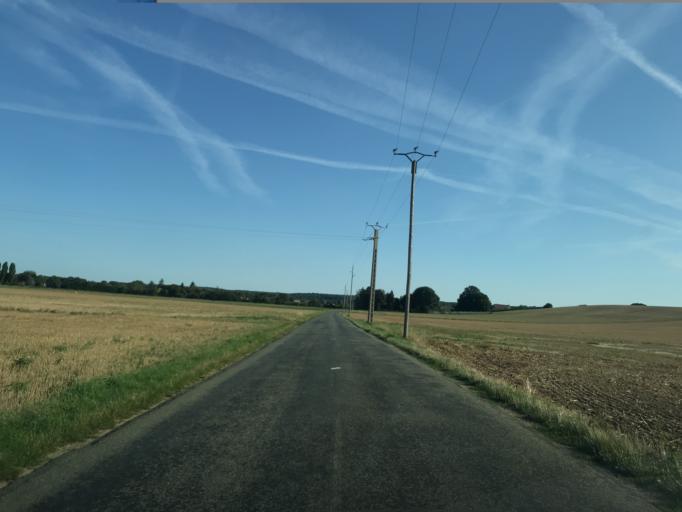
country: FR
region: Haute-Normandie
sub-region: Departement de l'Eure
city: Houlbec-Cocherel
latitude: 49.0588
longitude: 1.2978
